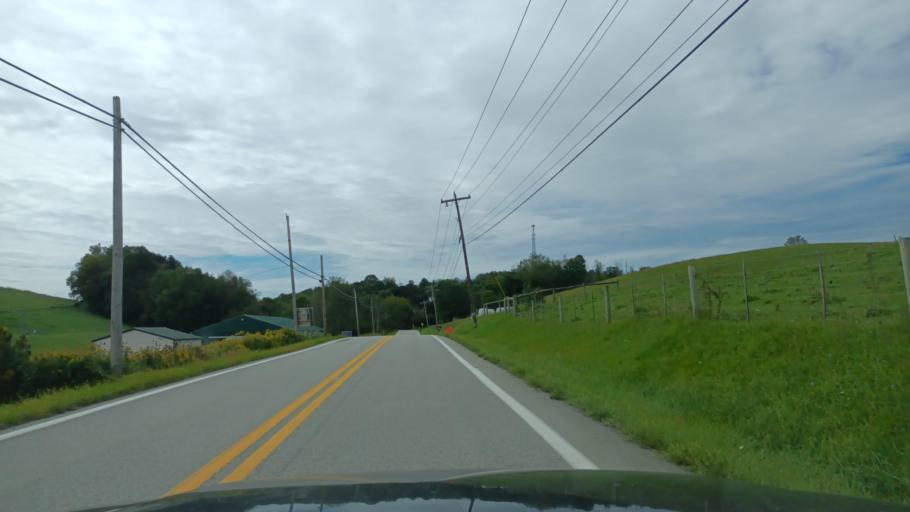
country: US
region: West Virginia
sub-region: Taylor County
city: Grafton
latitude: 39.3300
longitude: -80.0957
